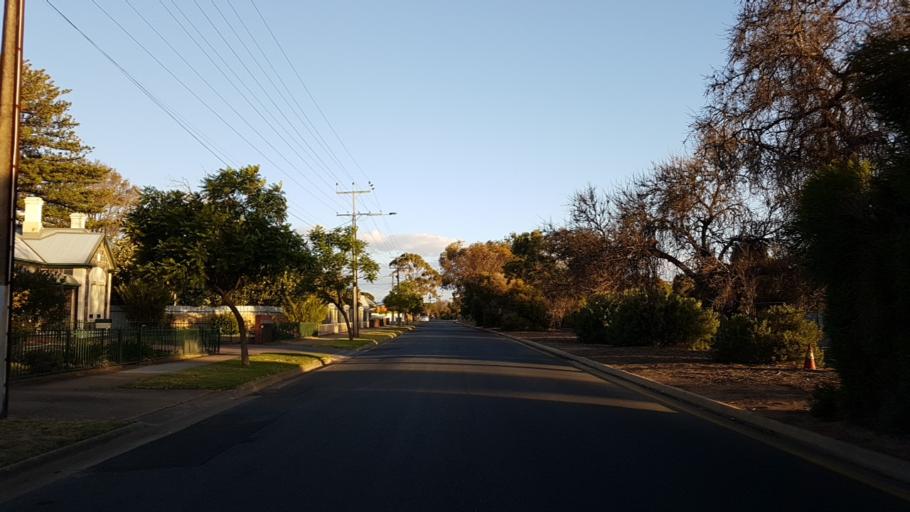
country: AU
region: South Australia
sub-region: Port Adelaide Enfield
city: Alberton
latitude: -34.8642
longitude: 138.5237
